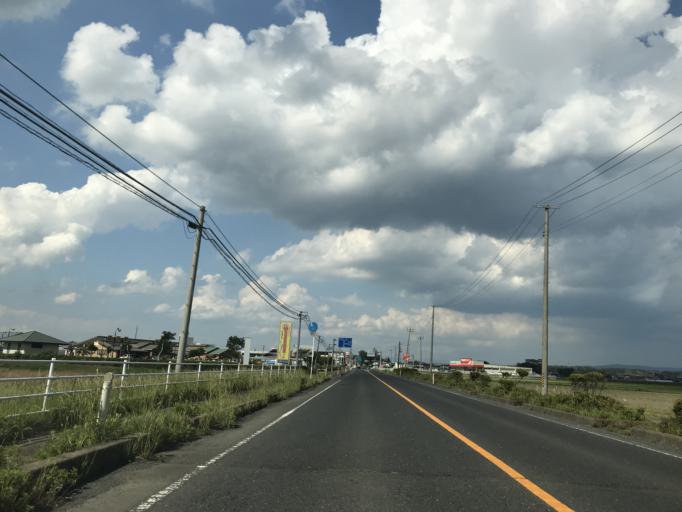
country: JP
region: Miyagi
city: Wakuya
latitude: 38.6253
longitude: 141.1873
